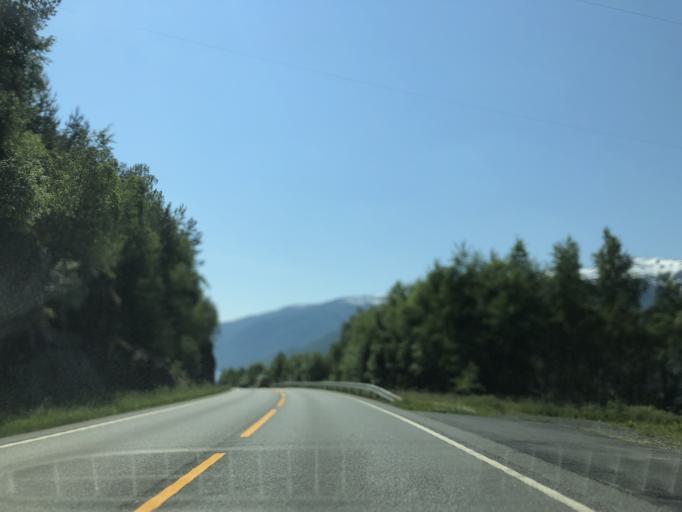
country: NO
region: Rogaland
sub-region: Sauda
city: Sauda
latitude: 59.8299
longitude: 6.2519
